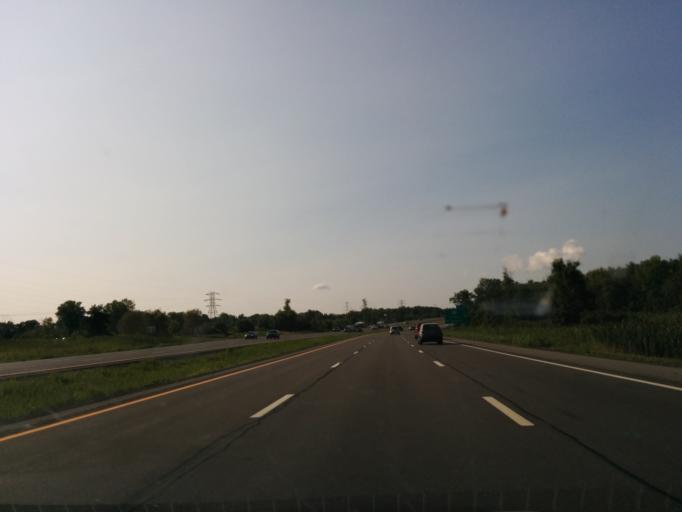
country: US
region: New York
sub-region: Onondaga County
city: North Syracuse
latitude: 43.1703
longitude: -76.1129
